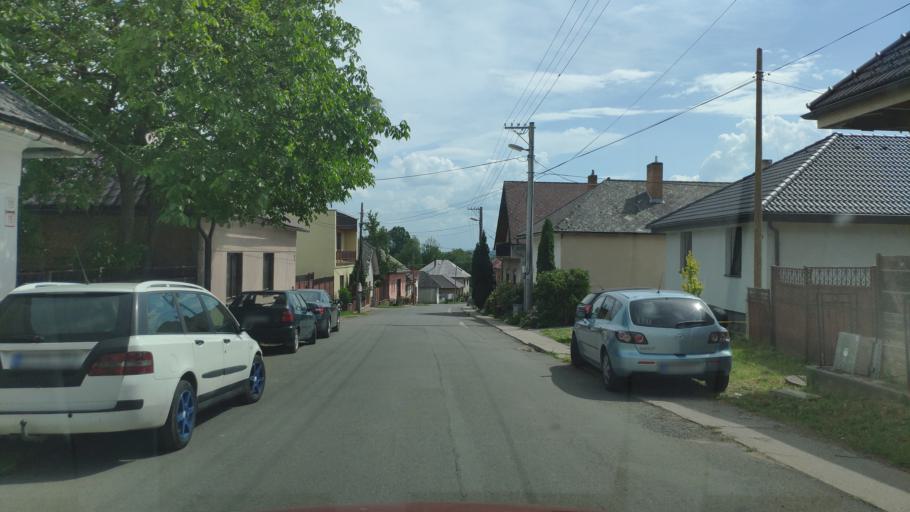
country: SK
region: Kosicky
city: Medzev
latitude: 48.7098
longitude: 20.9743
